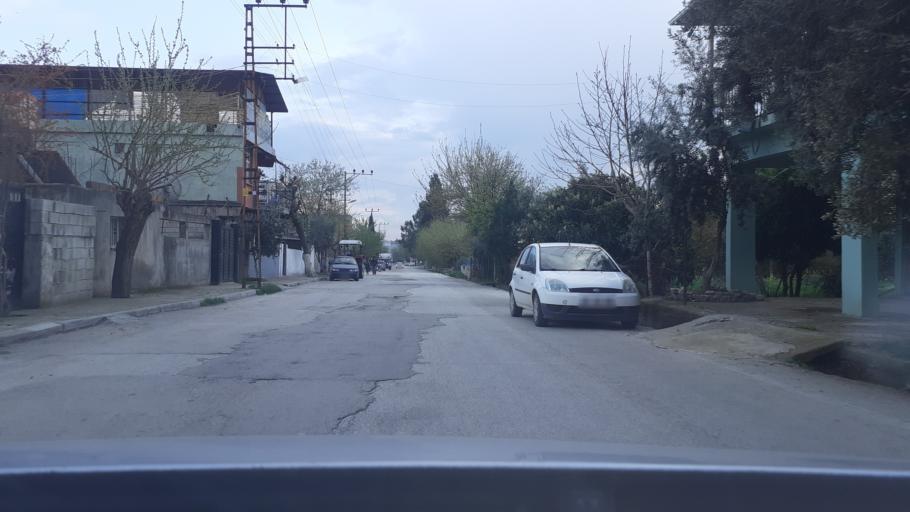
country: TR
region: Hatay
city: Kirikhan
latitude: 36.4861
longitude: 36.3504
